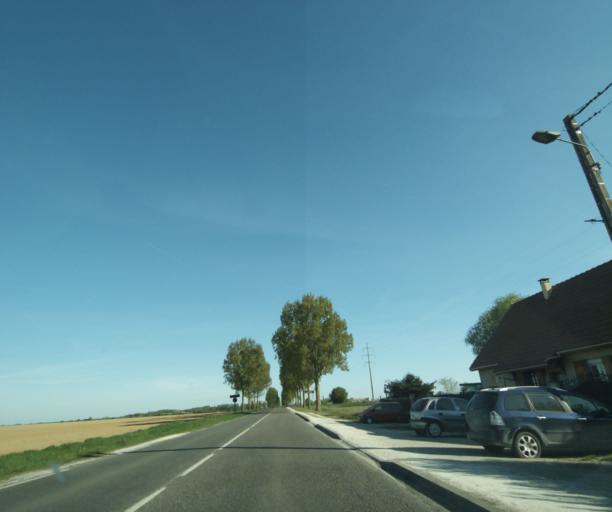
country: FR
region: Ile-de-France
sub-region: Departement de Seine-et-Marne
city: Bailly-Carrois
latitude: 48.5748
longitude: 2.9949
